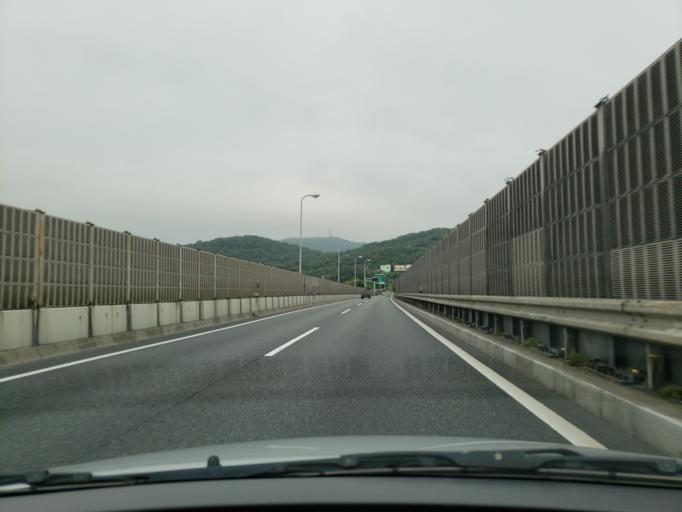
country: JP
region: Hyogo
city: Himeji
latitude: 34.8172
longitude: 134.6492
